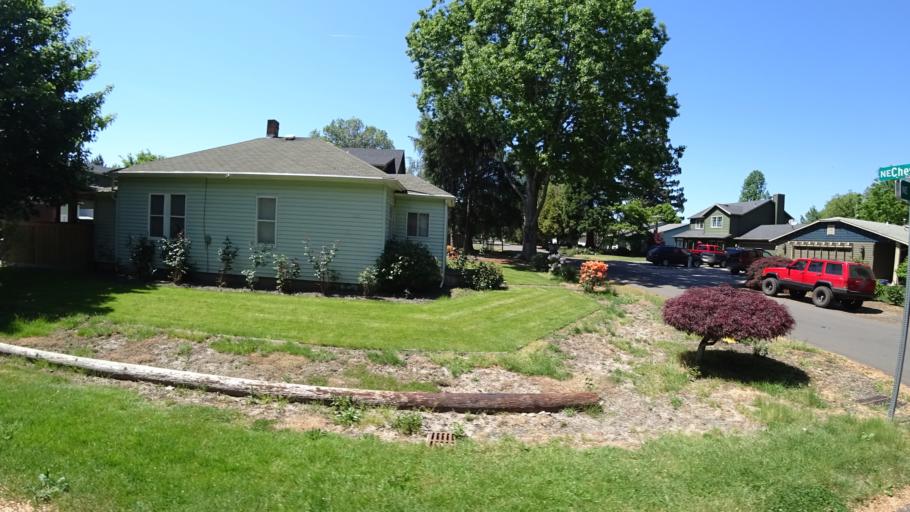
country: US
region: Oregon
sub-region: Washington County
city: Rockcreek
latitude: 45.5277
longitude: -122.9134
